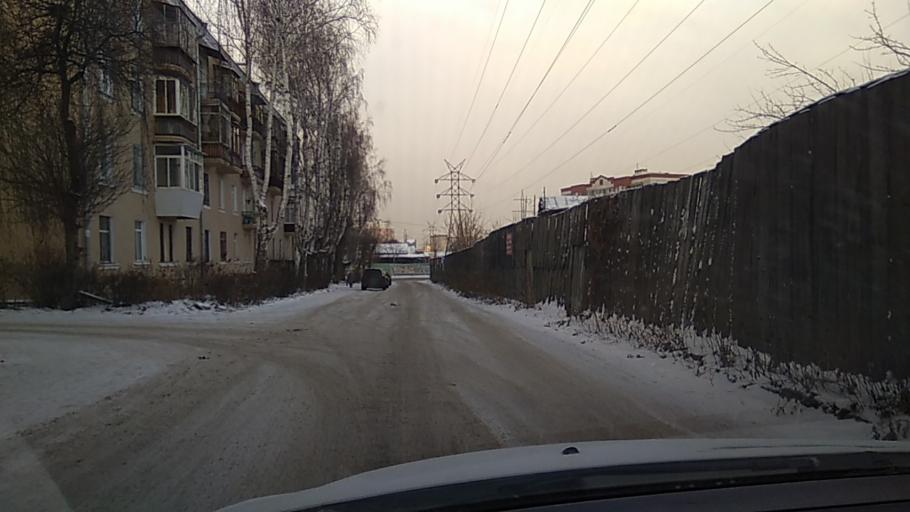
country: RU
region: Sverdlovsk
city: Yekaterinburg
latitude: 56.8877
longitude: 60.6195
